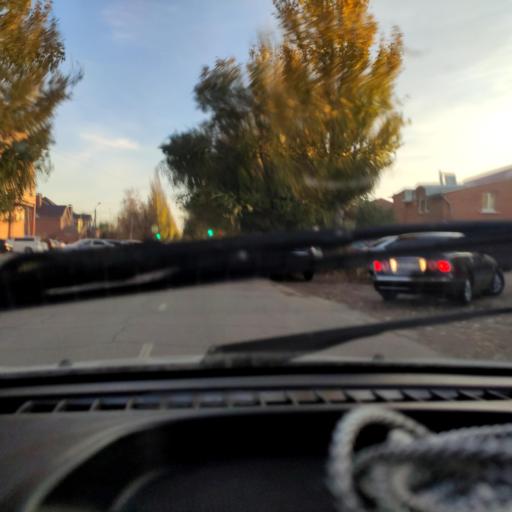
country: RU
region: Samara
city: Tol'yatti
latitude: 53.5370
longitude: 49.4168
